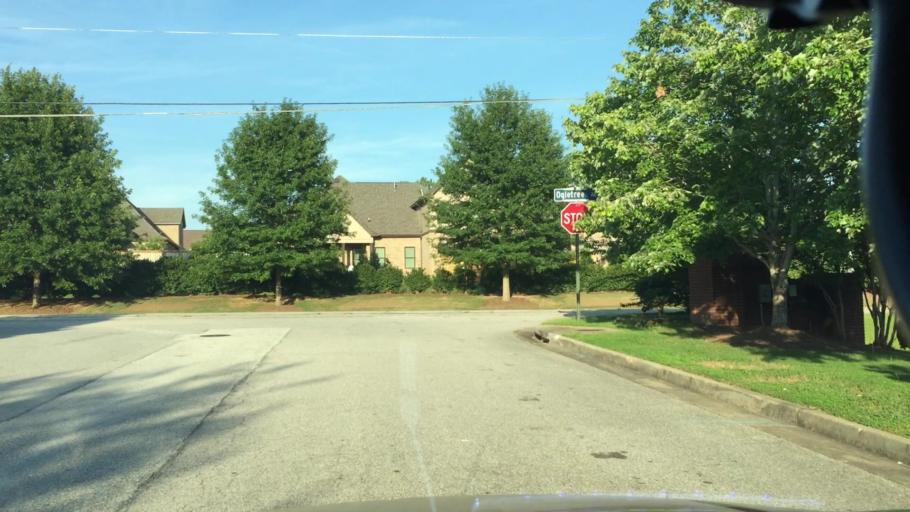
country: US
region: Alabama
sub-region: Lee County
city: Auburn
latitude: 32.5730
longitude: -85.4391
